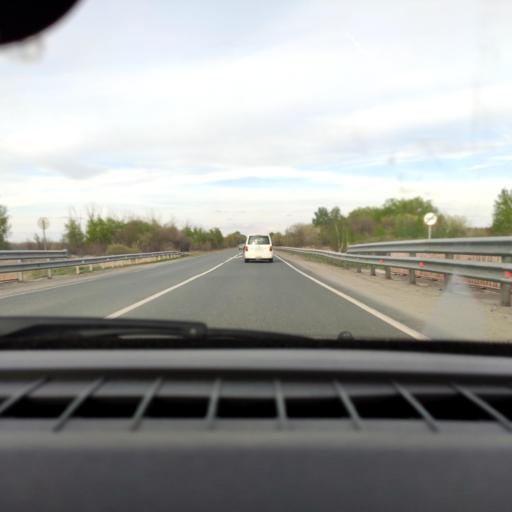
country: RU
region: Samara
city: Georgiyevka
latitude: 53.2752
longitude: 51.0598
